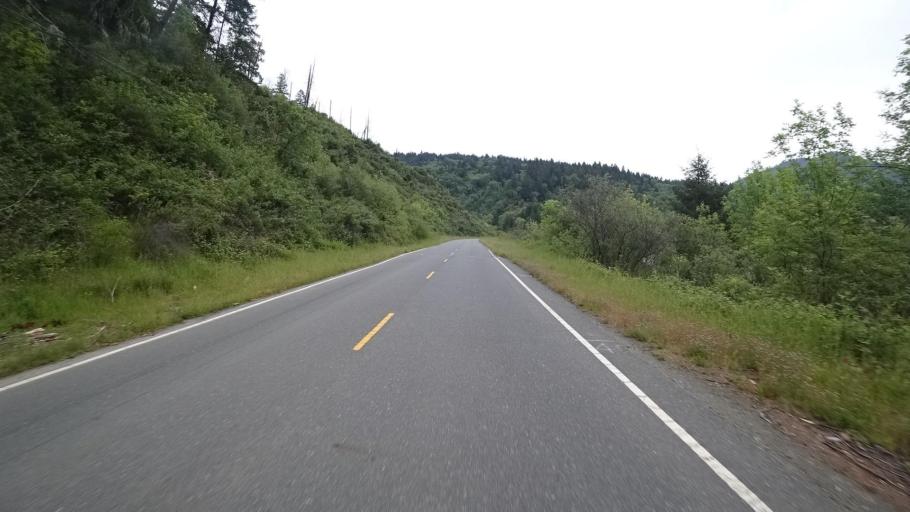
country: US
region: California
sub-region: Humboldt County
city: Willow Creek
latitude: 41.0984
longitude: -123.7119
